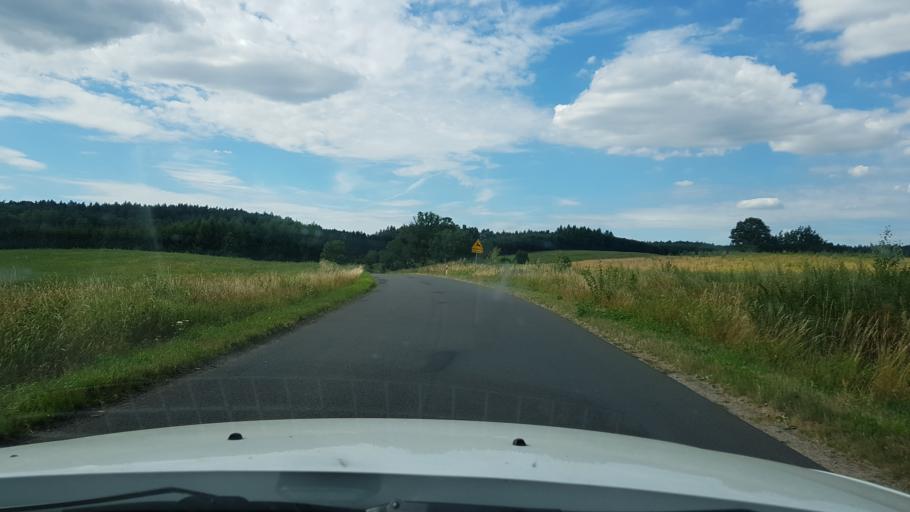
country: PL
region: West Pomeranian Voivodeship
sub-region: Powiat drawski
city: Zlocieniec
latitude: 53.4849
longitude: 16.0444
